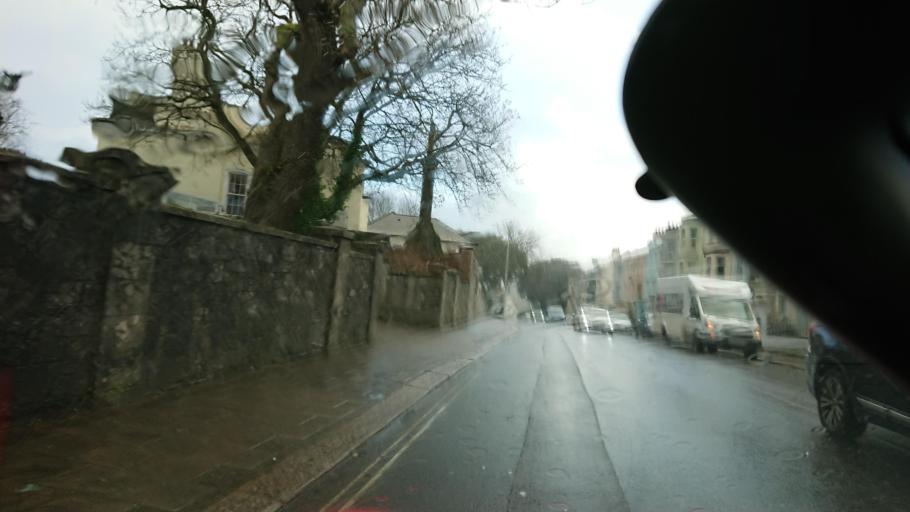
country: GB
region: England
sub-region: Cornwall
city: Millbrook
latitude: 50.3774
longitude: -4.1683
